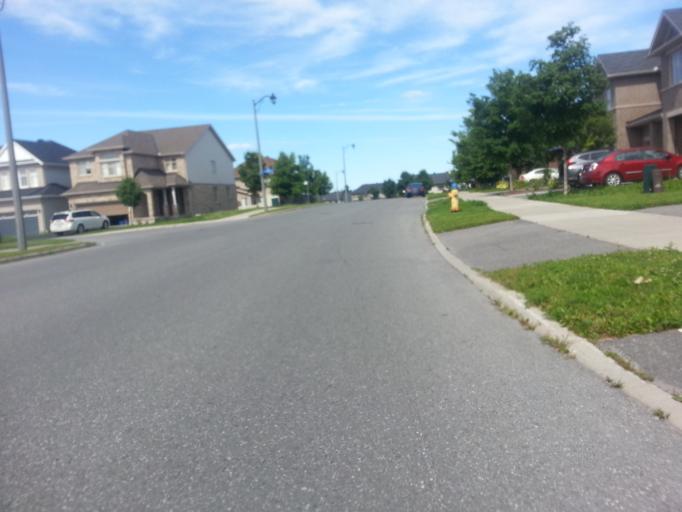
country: CA
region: Ontario
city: Bells Corners
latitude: 45.3221
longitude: -75.9342
